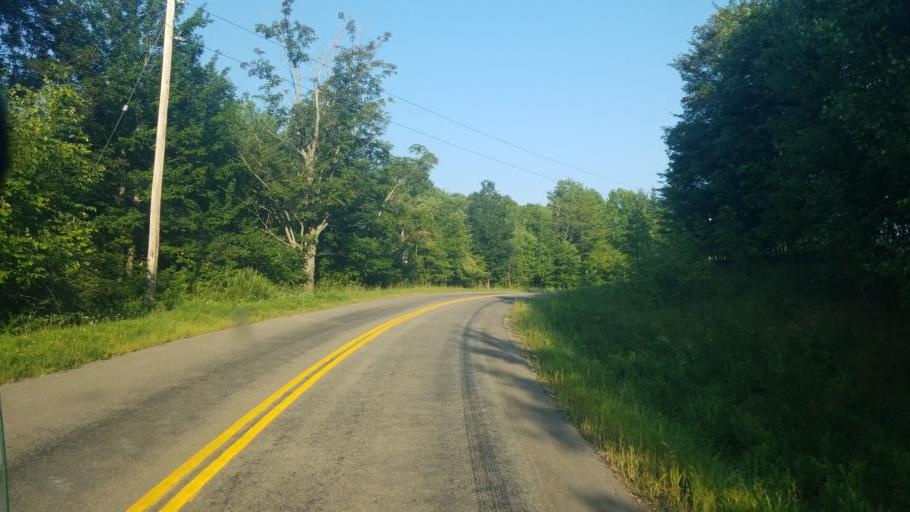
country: US
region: Pennsylvania
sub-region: Tioga County
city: Westfield
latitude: 42.0664
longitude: -77.6317
